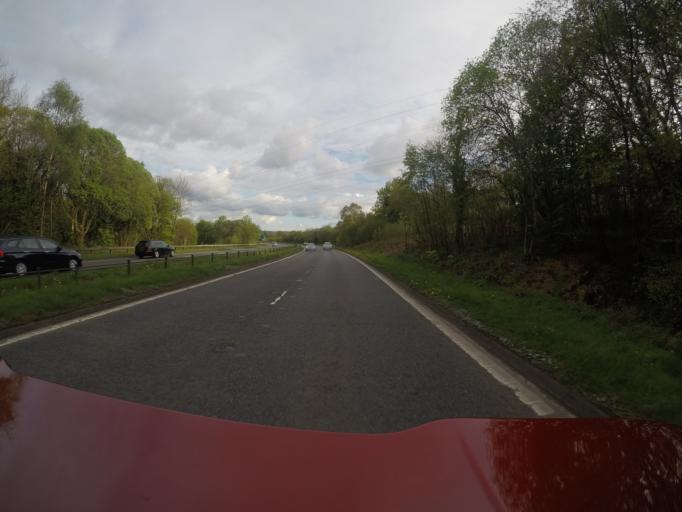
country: GB
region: Scotland
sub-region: West Dunbartonshire
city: Renton
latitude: 55.9655
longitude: -4.5875
